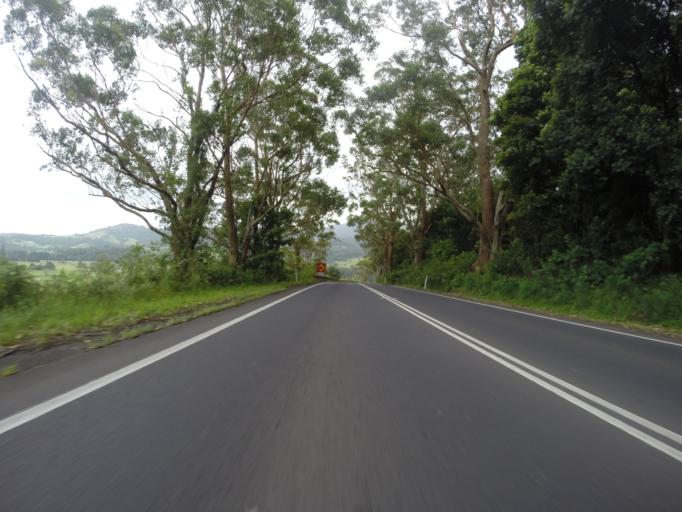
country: AU
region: New South Wales
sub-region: Kiama
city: Gerringong
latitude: -34.7415
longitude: 150.7712
